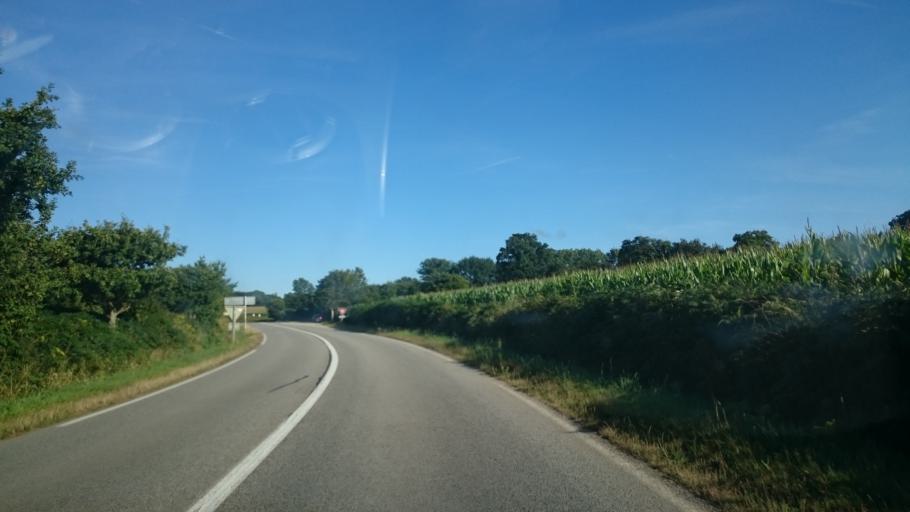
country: FR
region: Lower Normandy
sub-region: Departement de la Manche
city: Martinvast
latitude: 49.5768
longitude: -1.7076
